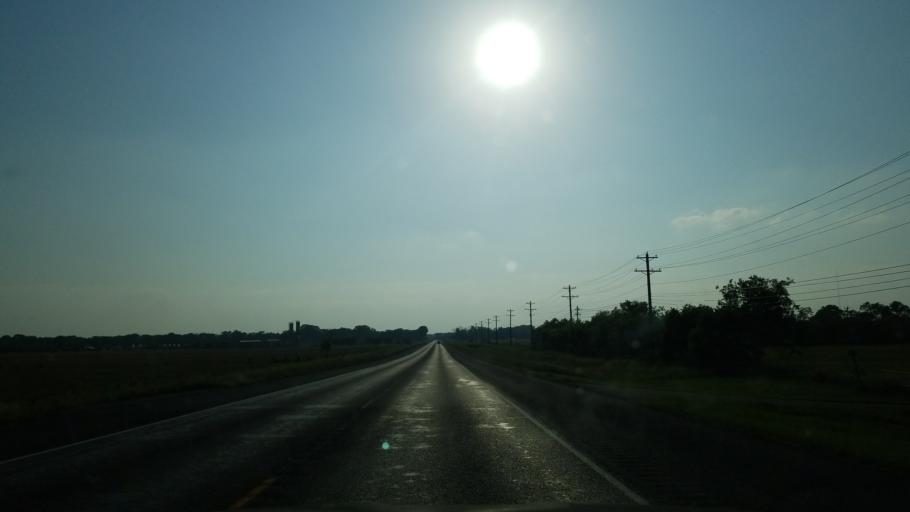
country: US
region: Texas
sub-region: Denton County
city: Aubrey
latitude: 33.3053
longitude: -97.0297
